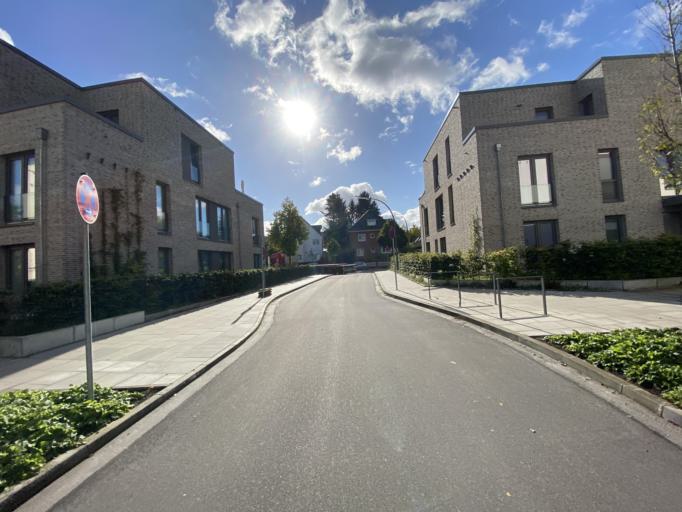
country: DE
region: Hamburg
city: Hamburg-Nord
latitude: 53.5943
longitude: 9.9712
